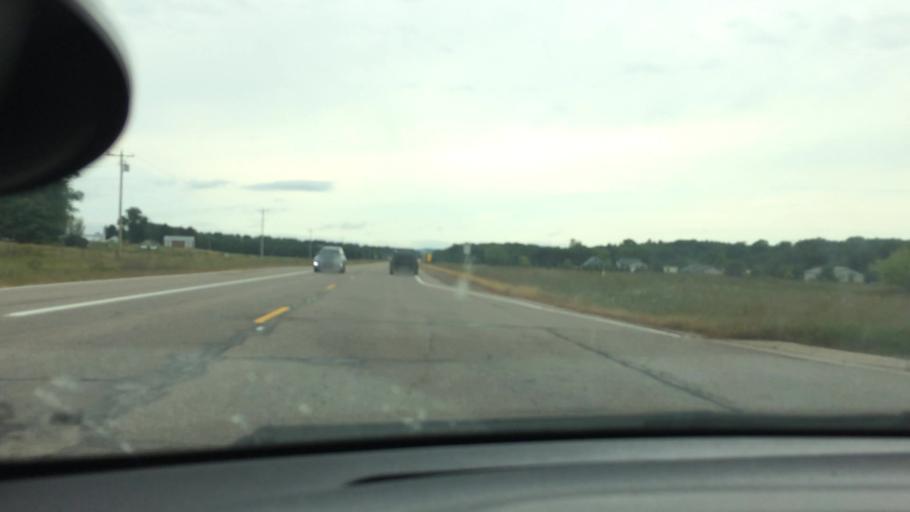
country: US
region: Wisconsin
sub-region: Trempealeau County
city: Osseo
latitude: 44.5866
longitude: -91.1451
